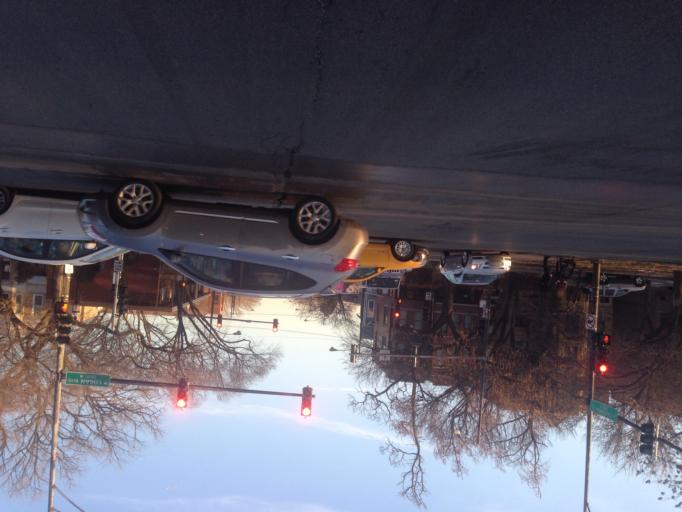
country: US
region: Illinois
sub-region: Cook County
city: Lincolnwood
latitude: 41.9283
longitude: -87.6975
